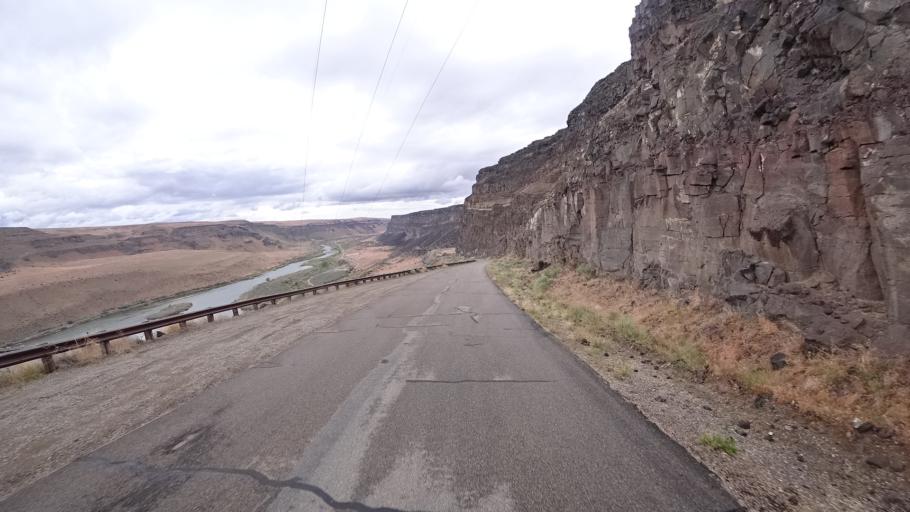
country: US
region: Idaho
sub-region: Owyhee County
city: Murphy
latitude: 43.2428
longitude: -116.3712
